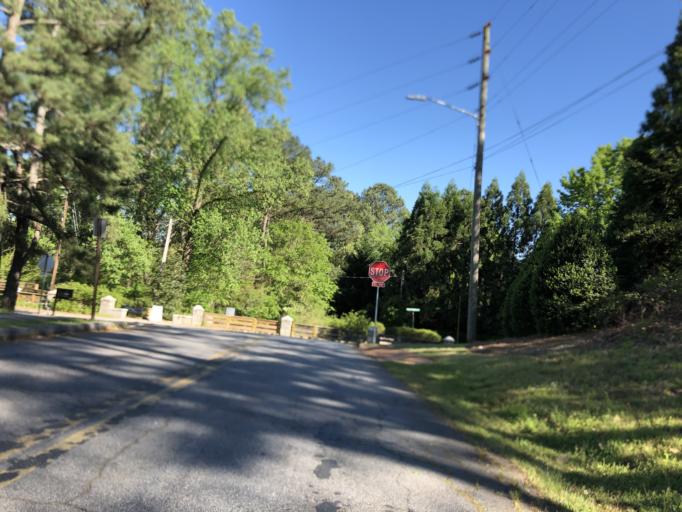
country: US
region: Georgia
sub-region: DeKalb County
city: North Druid Hills
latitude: 33.8062
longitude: -84.3057
